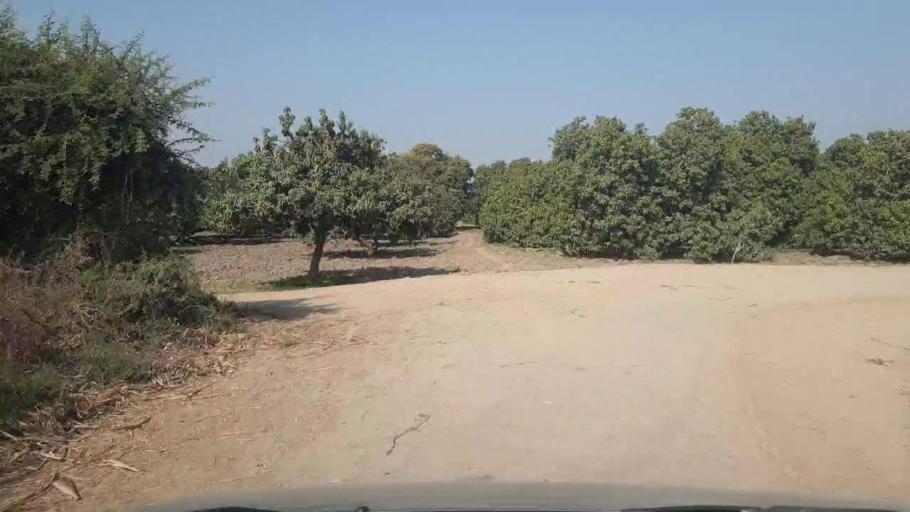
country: PK
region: Sindh
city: Mirwah Gorchani
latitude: 25.2567
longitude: 69.0915
